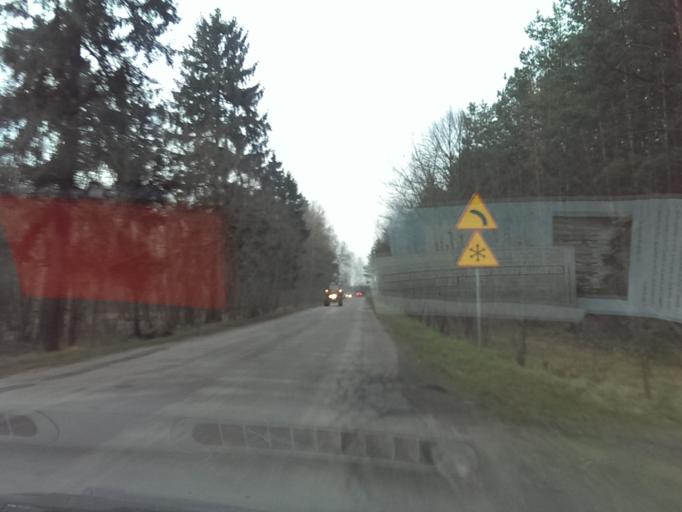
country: PL
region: Kujawsko-Pomorskie
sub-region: Powiat nakielski
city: Szubin
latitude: 53.0781
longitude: 17.7299
